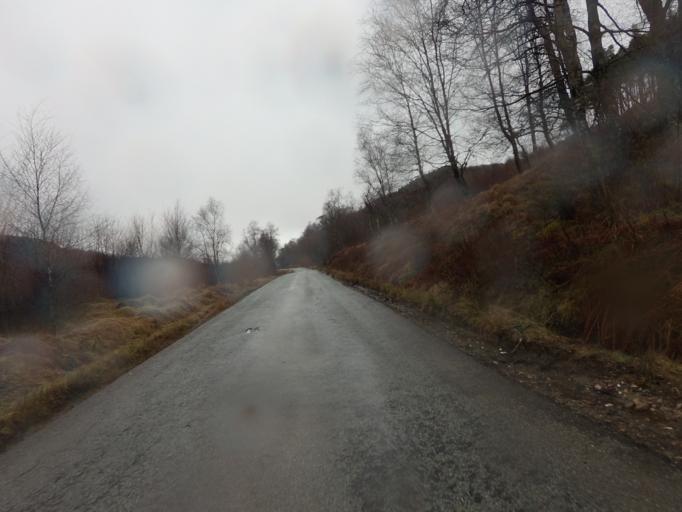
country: GB
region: Scotland
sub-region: West Dunbartonshire
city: Balloch
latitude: 56.2392
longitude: -4.5662
